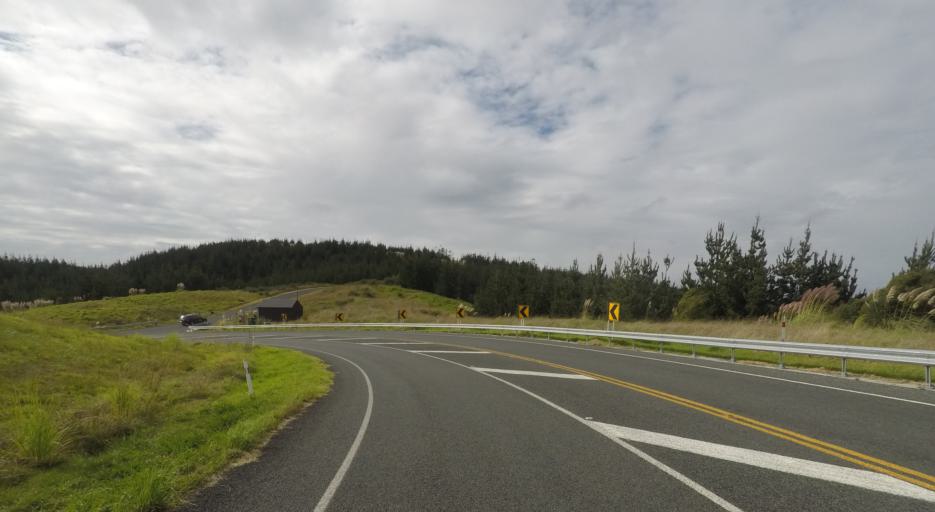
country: NZ
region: Auckland
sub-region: Auckland
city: Rothesay Bay
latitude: -36.6562
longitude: 174.6986
